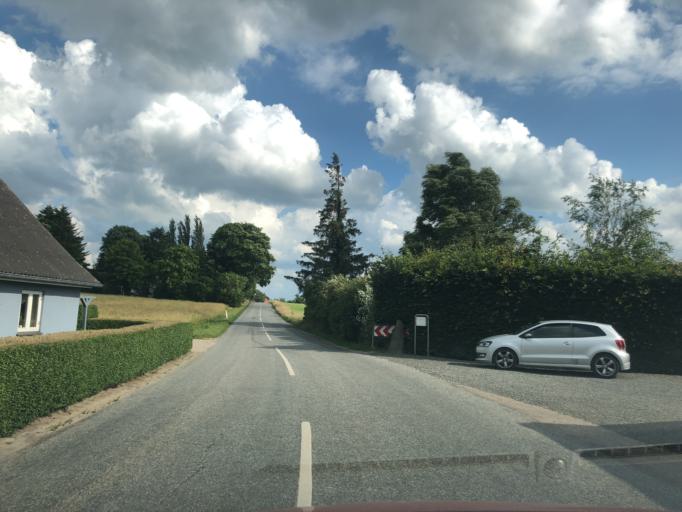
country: DK
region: Zealand
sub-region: Stevns Kommune
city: Harlev
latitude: 55.2893
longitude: 12.2170
